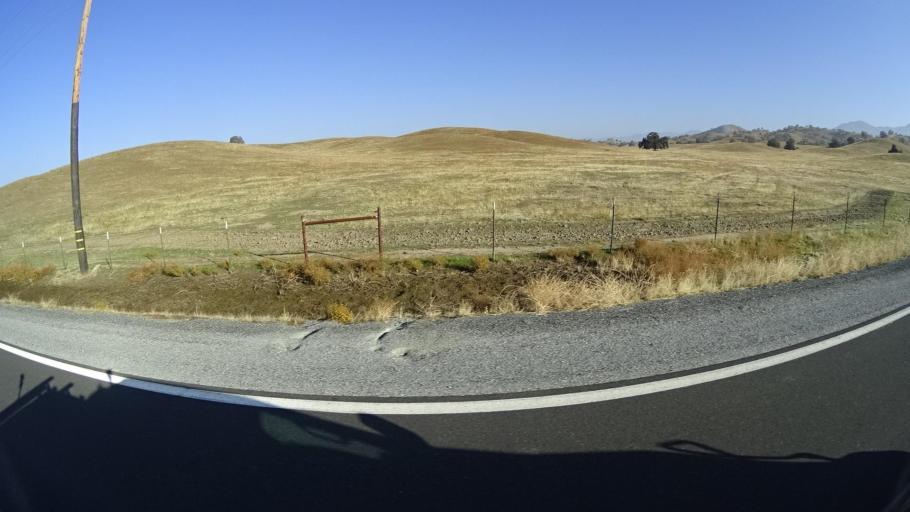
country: US
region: California
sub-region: Tulare County
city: Richgrove
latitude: 35.7416
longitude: -118.8759
